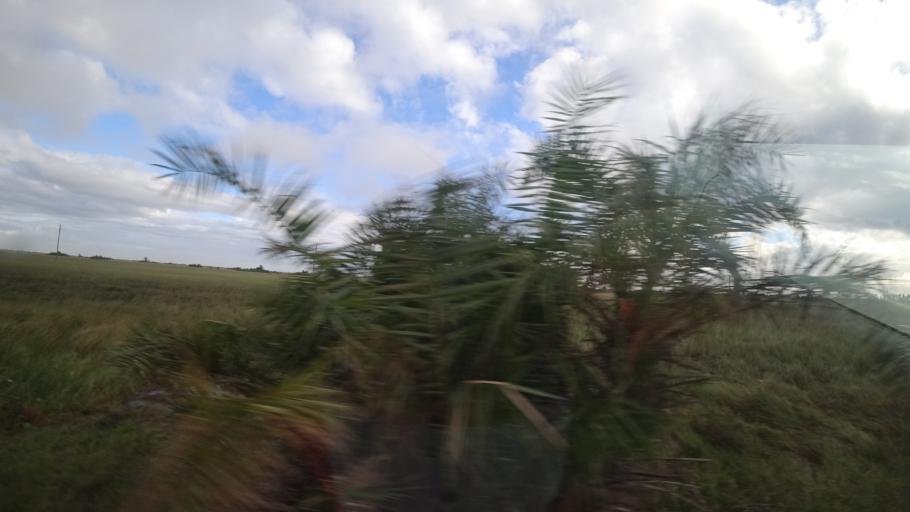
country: MZ
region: Sofala
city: Beira
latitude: -19.7277
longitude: 34.9871
